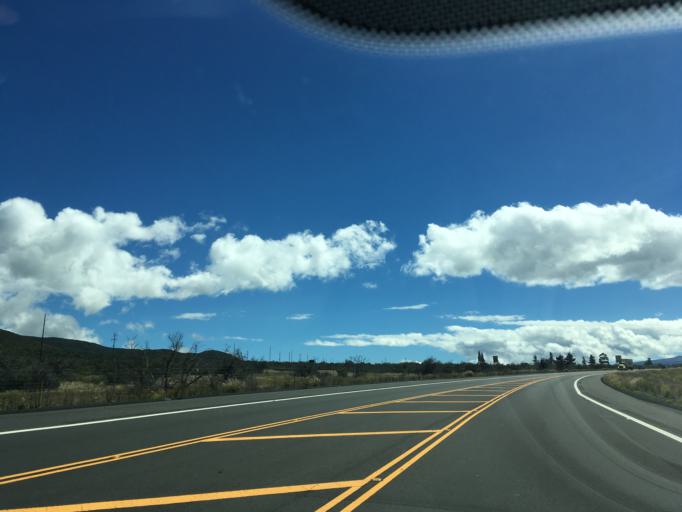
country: US
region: Hawaii
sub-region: Hawaii County
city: Waimea
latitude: 19.7572
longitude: -155.5313
